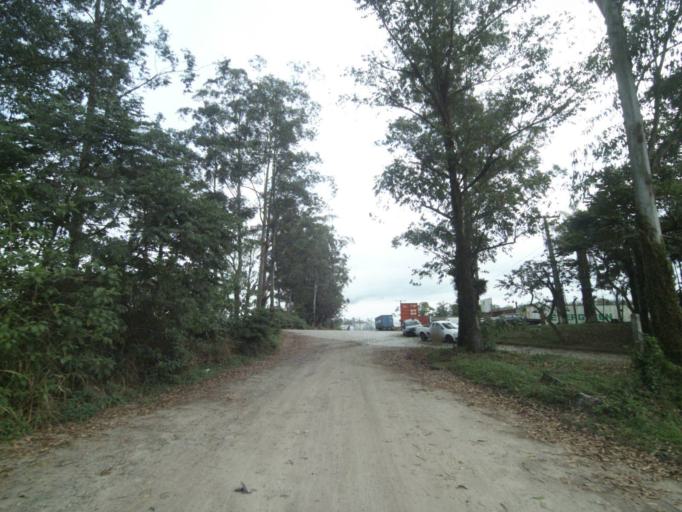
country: BR
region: Parana
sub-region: Paranagua
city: Paranagua
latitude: -25.5381
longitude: -48.5580
